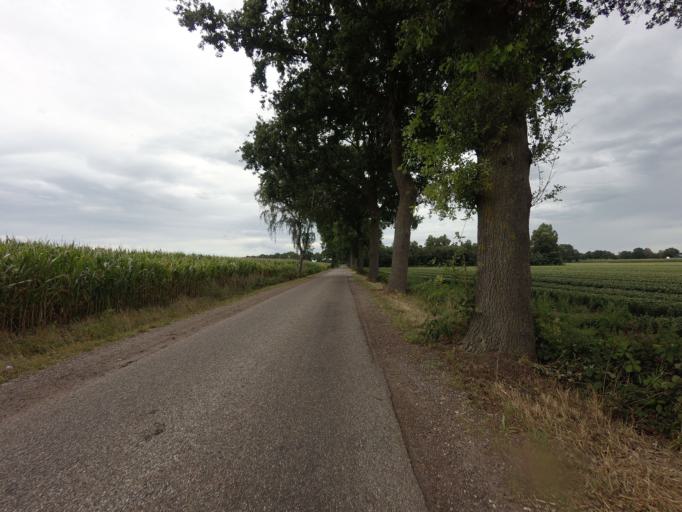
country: NL
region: Overijssel
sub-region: Gemeente Raalte
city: Raalte
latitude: 52.3603
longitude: 6.3554
